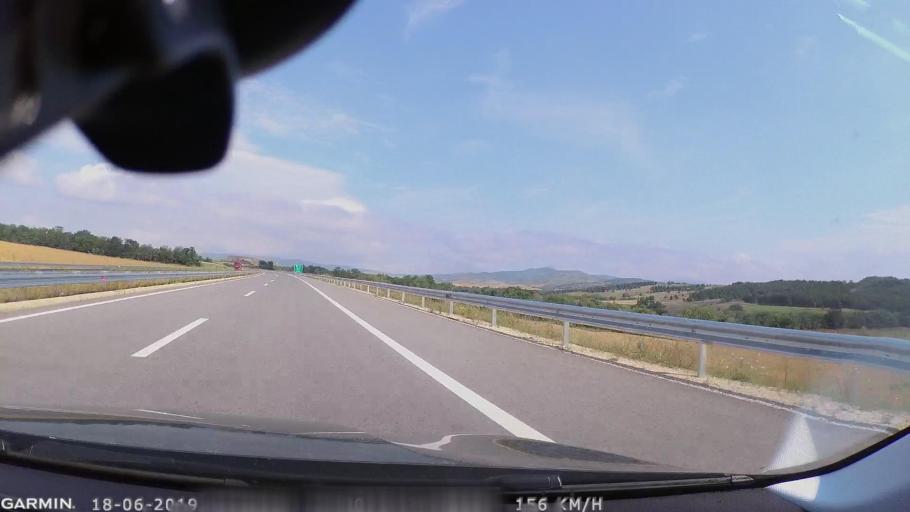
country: MK
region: Sveti Nikole
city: Gorobinci
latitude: 41.9084
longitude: 21.9046
